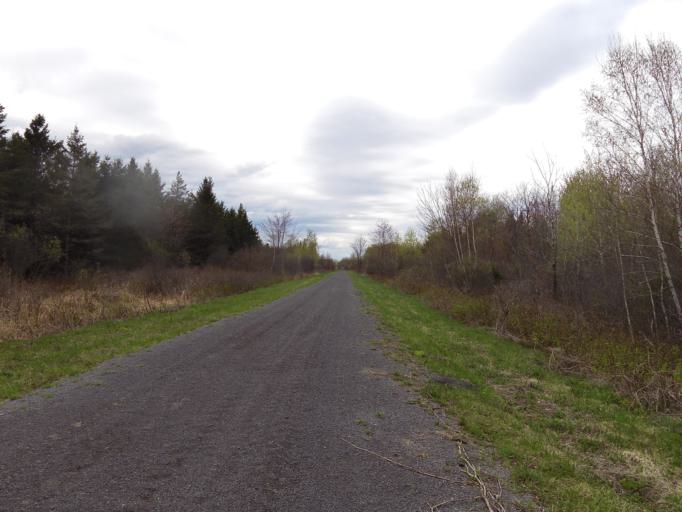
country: CA
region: Ontario
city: Hawkesbury
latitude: 45.5442
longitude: -74.7711
